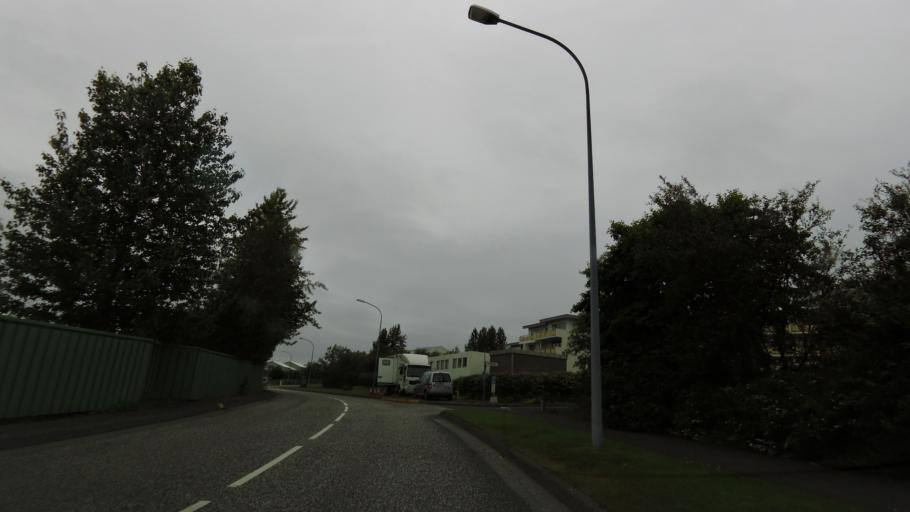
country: IS
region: Capital Region
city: Reykjavik
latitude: 64.1073
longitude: -21.8579
